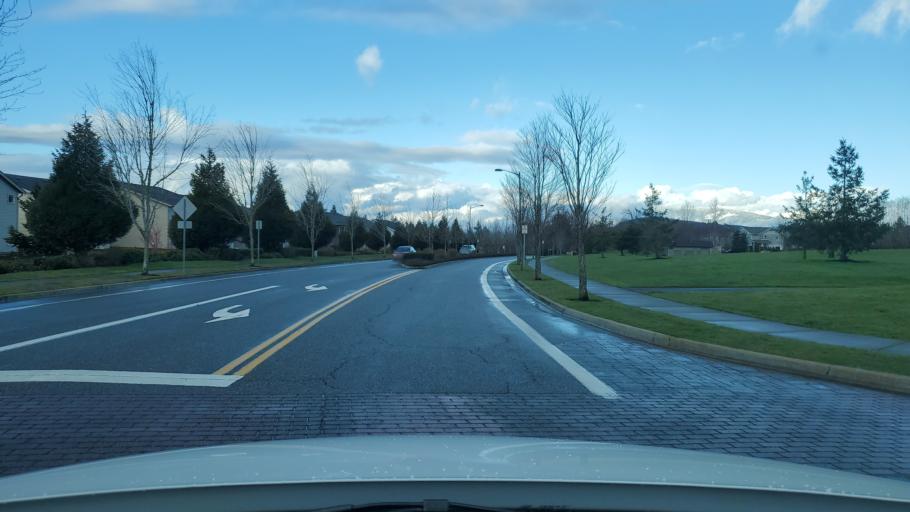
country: US
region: Washington
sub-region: Skagit County
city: Big Lake
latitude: 48.4268
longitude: -122.2783
